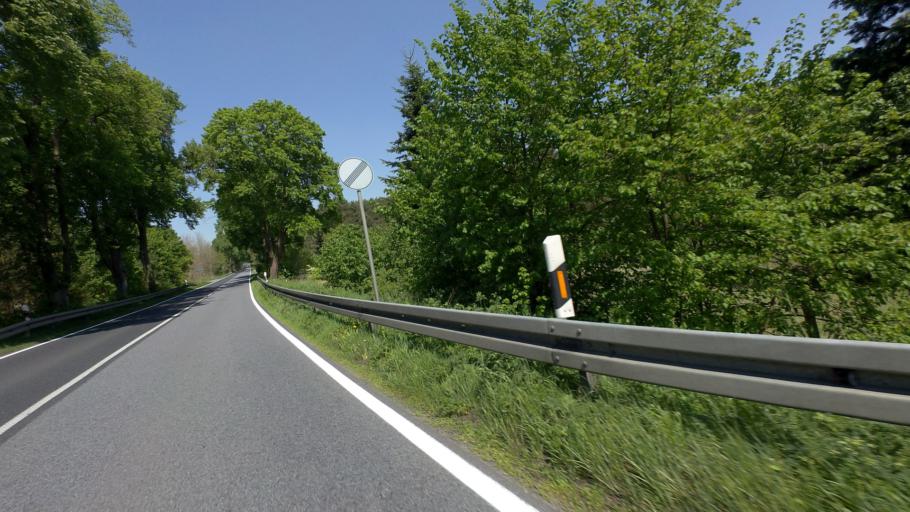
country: DE
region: Brandenburg
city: Furstenberg
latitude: 53.1498
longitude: 13.1504
